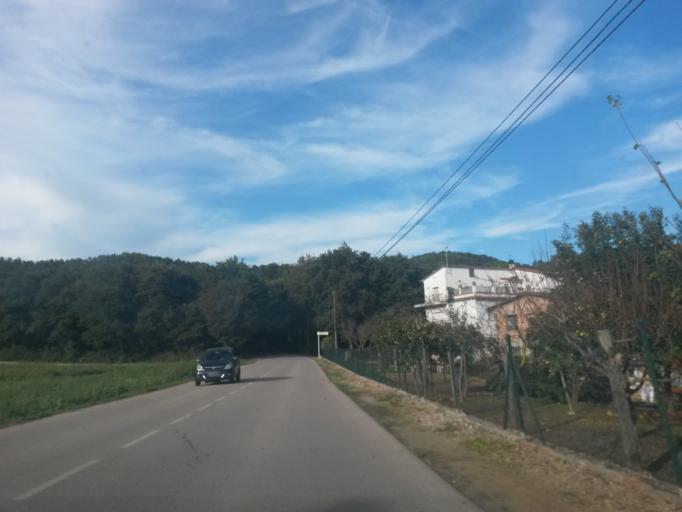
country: ES
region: Catalonia
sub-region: Provincia de Girona
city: Angles
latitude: 41.9646
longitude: 2.6381
